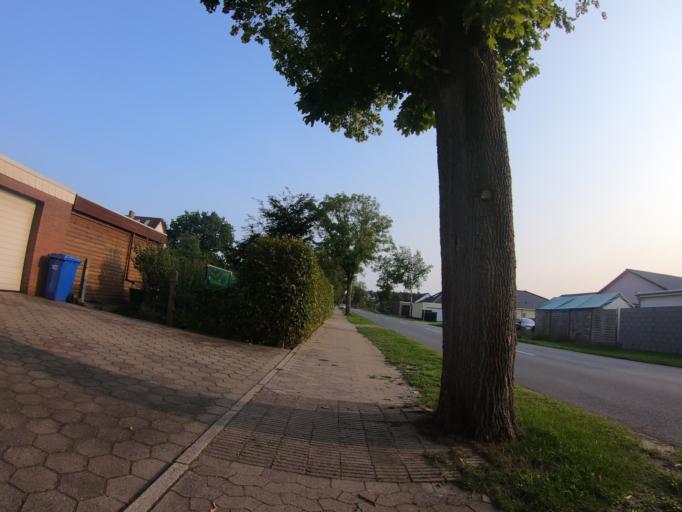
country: DE
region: Lower Saxony
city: Leiferde
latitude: 52.4541
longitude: 10.4280
